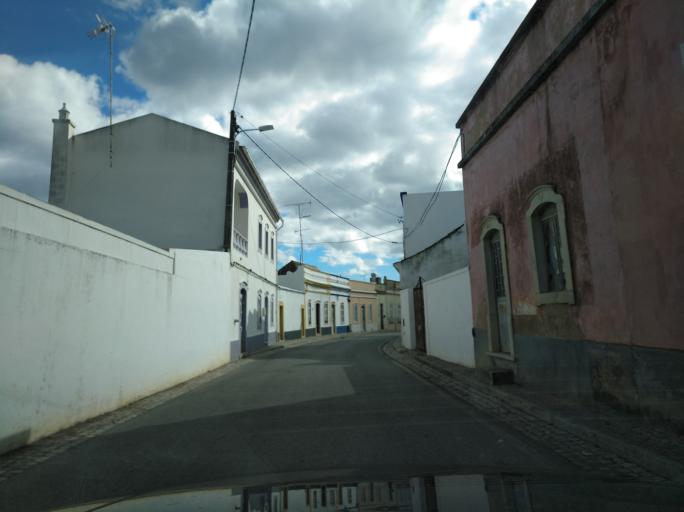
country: PT
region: Faro
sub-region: Tavira
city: Luz
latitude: 37.0938
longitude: -7.7042
